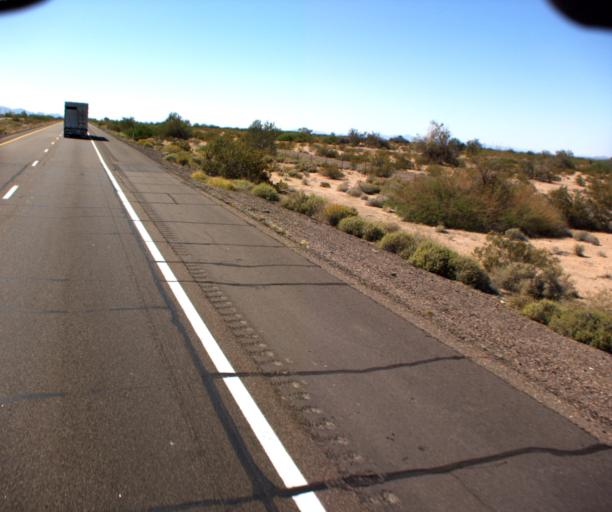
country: US
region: Arizona
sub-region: Yuma County
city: Wellton
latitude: 32.8216
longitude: -113.4673
